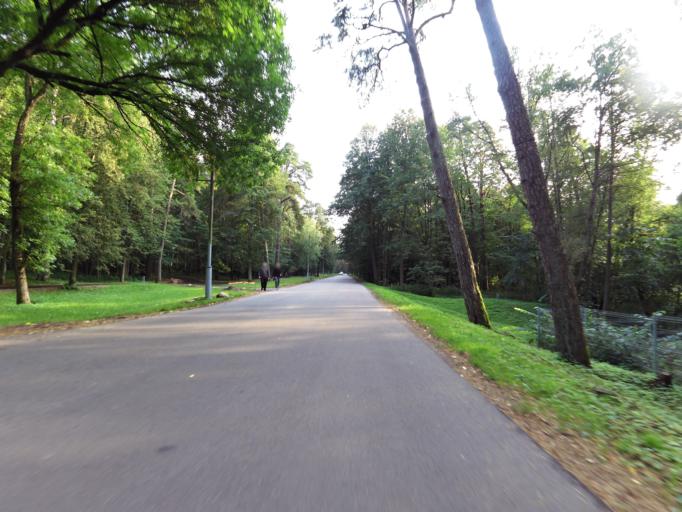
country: LT
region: Vilnius County
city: Vilkpede
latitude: 54.6811
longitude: 25.2341
